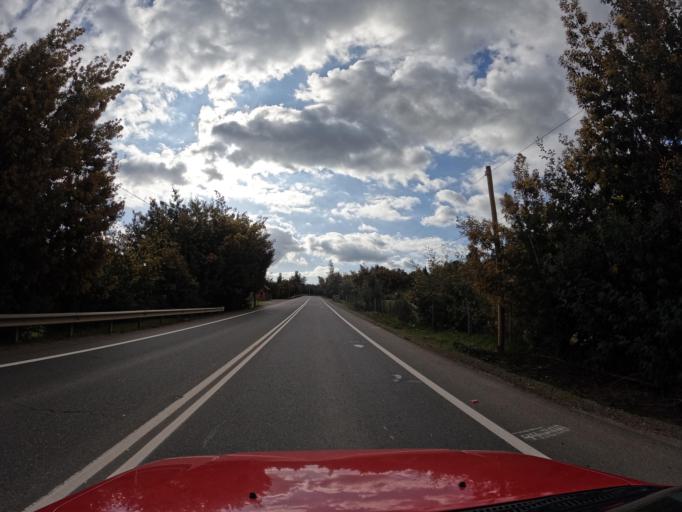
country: CL
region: Maule
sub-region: Provincia de Talca
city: Constitucion
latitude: -35.5549
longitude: -72.1414
